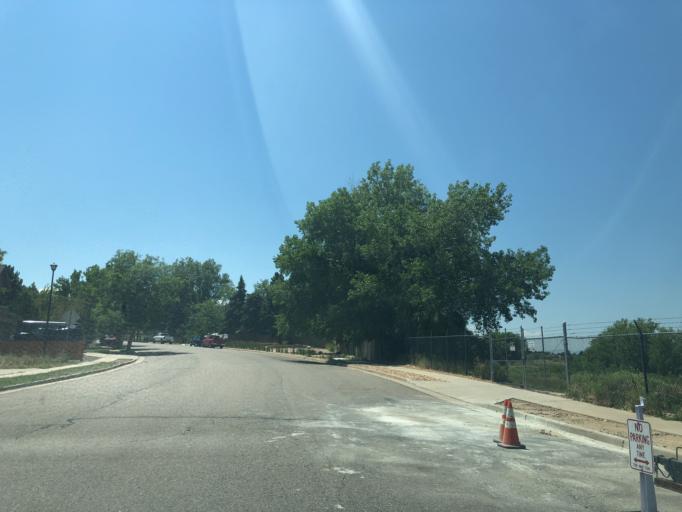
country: US
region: Colorado
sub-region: Arapahoe County
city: Dove Valley
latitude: 39.6303
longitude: -104.7712
